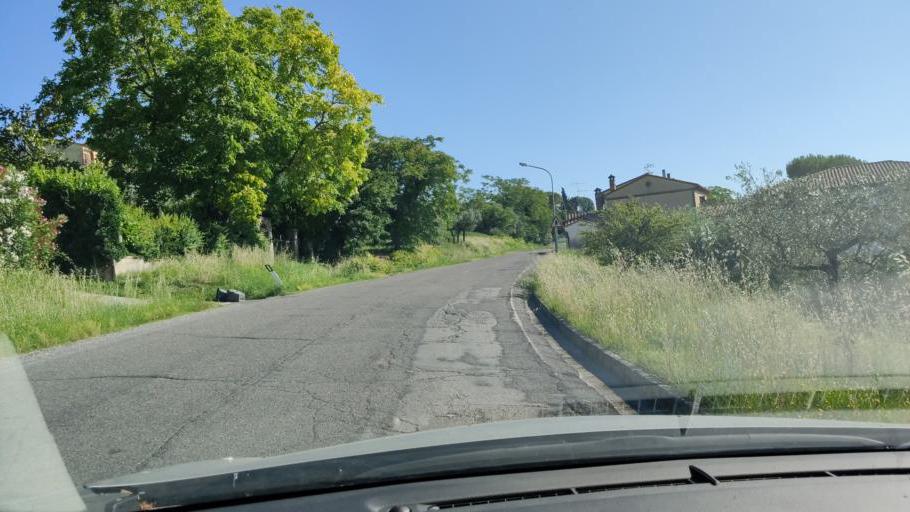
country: IT
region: Umbria
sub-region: Provincia di Terni
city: Avigliano Umbro
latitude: 42.6512
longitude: 12.4199
